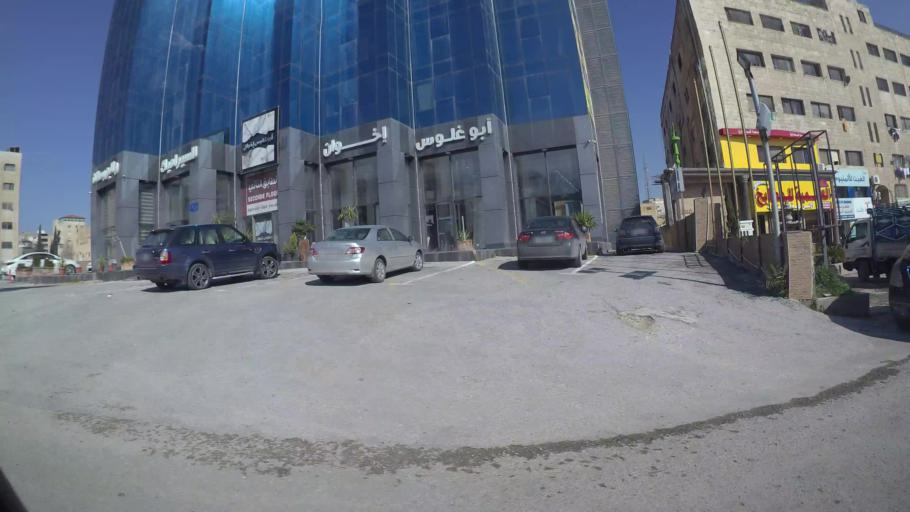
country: JO
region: Amman
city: Al Bunayyat ash Shamaliyah
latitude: 31.9113
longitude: 35.8959
